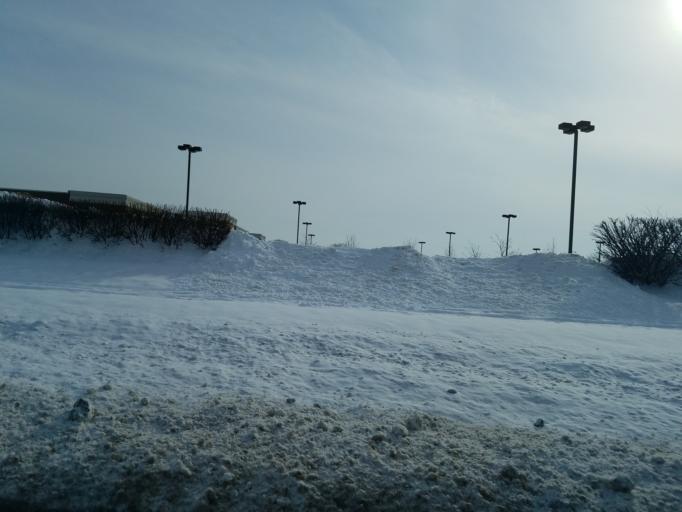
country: US
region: Illinois
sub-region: Cook County
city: Tinley Park
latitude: 41.5804
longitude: -87.7924
